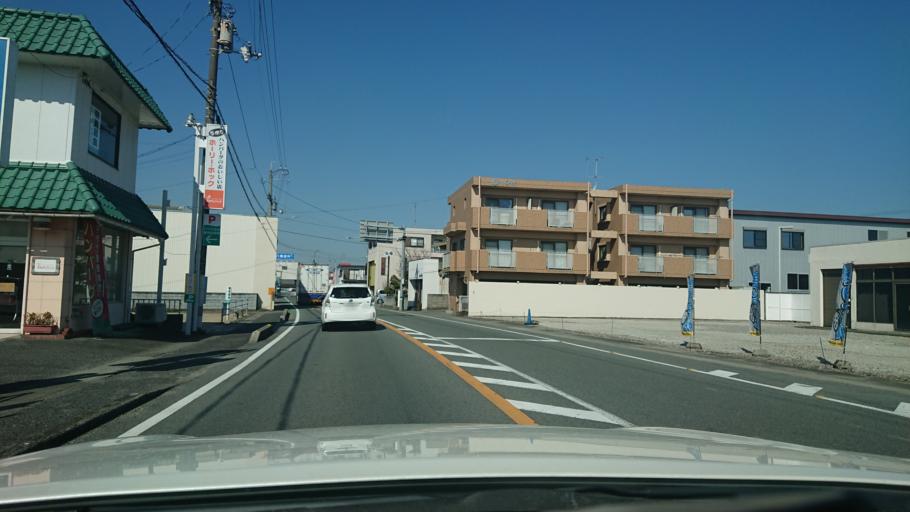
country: JP
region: Tokushima
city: Anan
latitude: 33.9620
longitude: 134.6227
